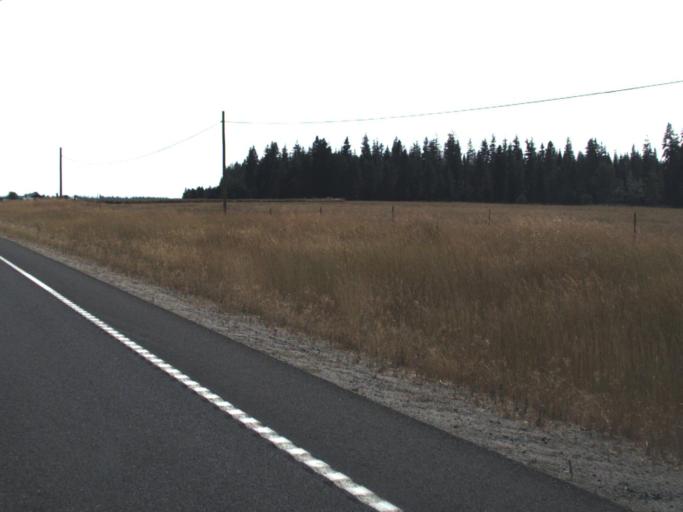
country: US
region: Washington
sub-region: Spokane County
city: Deer Park
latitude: 47.9856
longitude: -117.5340
